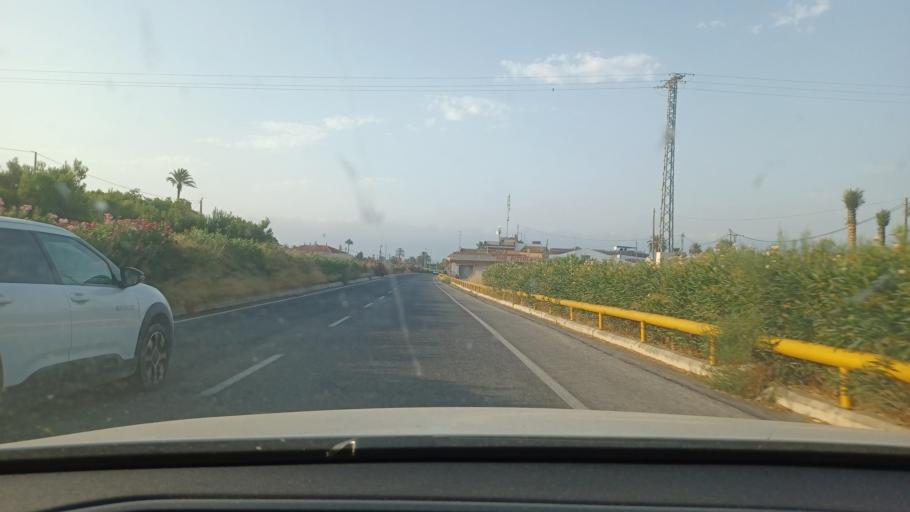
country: ES
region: Valencia
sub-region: Provincia de Alicante
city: Elche
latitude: 38.2253
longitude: -0.6989
